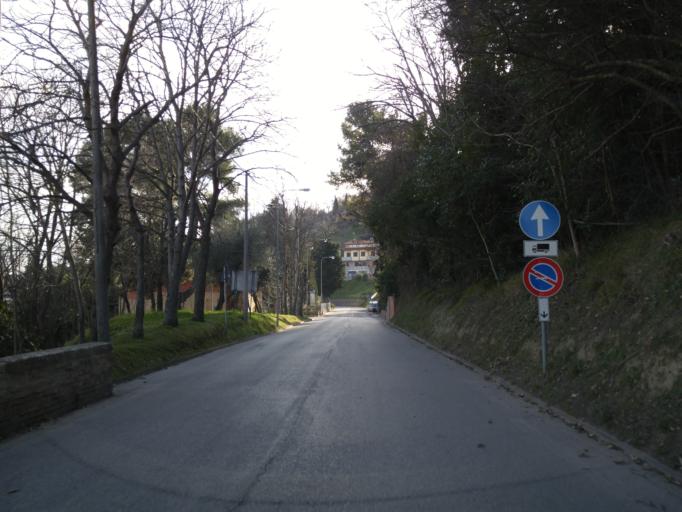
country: IT
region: The Marches
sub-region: Provincia di Pesaro e Urbino
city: Cartoceto
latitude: 43.7673
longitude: 12.8815
